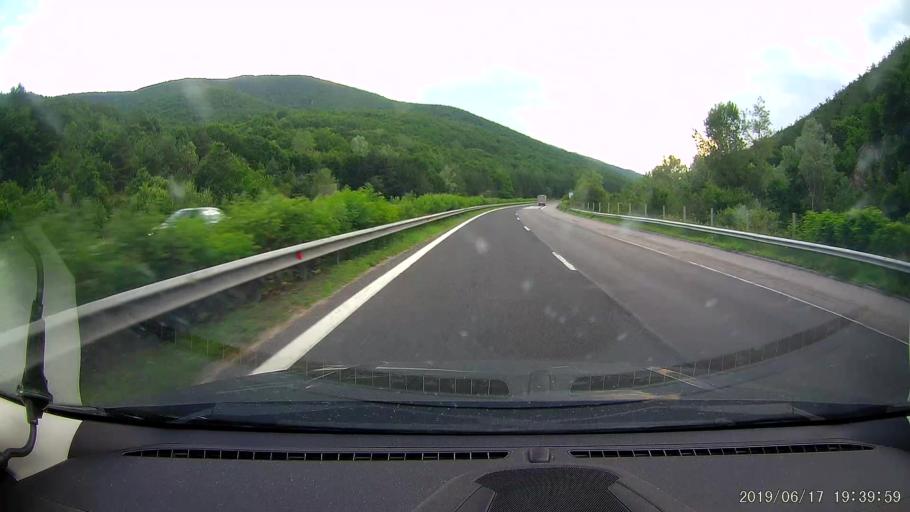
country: BG
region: Pazardzhik
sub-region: Obshtina Belovo
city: Belovo
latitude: 42.3262
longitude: 23.9678
